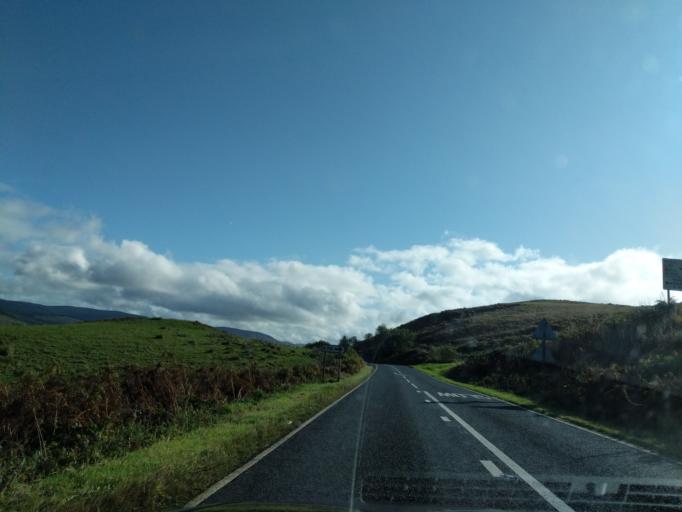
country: GB
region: Scotland
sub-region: Dumfries and Galloway
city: Moffat
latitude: 55.3621
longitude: -3.4775
